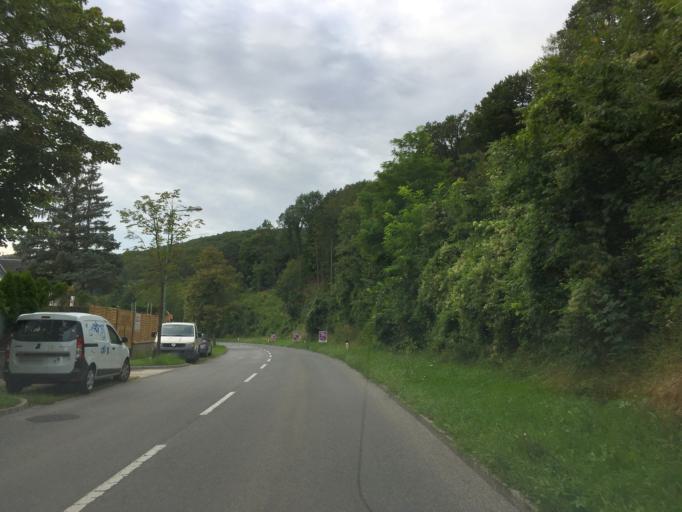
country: AT
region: Lower Austria
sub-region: Politischer Bezirk Tulln
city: Wordern
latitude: 48.3156
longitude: 16.2400
